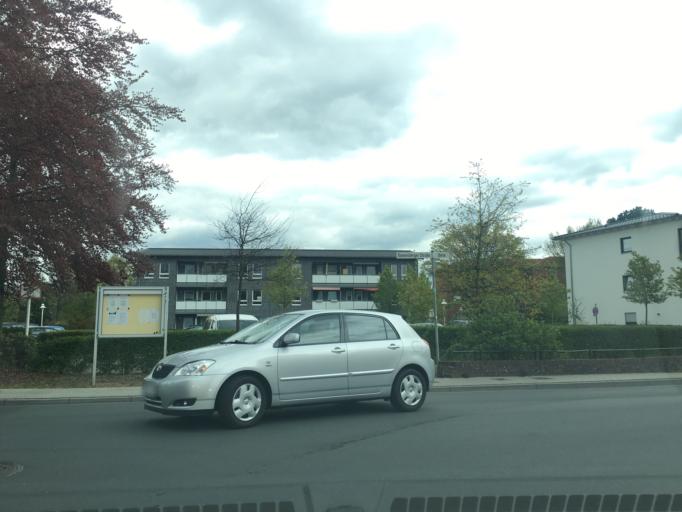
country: DE
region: North Rhine-Westphalia
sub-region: Regierungsbezirk Munster
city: Ascheberg
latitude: 51.7923
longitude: 7.6188
